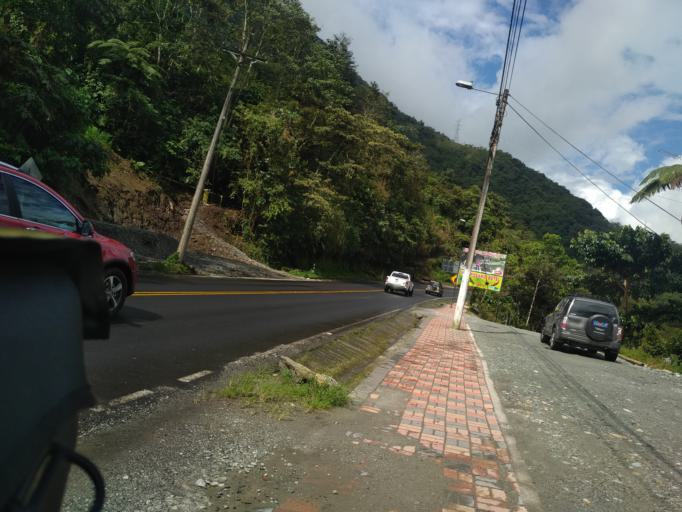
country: EC
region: Tungurahua
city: Banos
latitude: -1.4016
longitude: -78.2860
